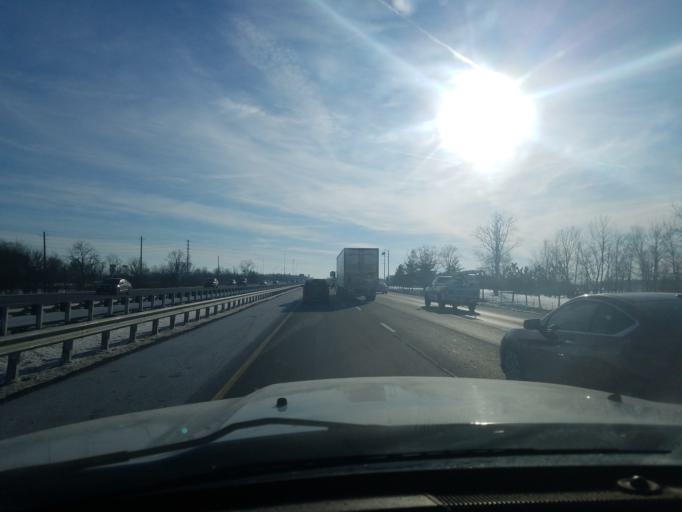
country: US
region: Indiana
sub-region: Madison County
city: Pendleton
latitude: 40.0123
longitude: -85.7681
